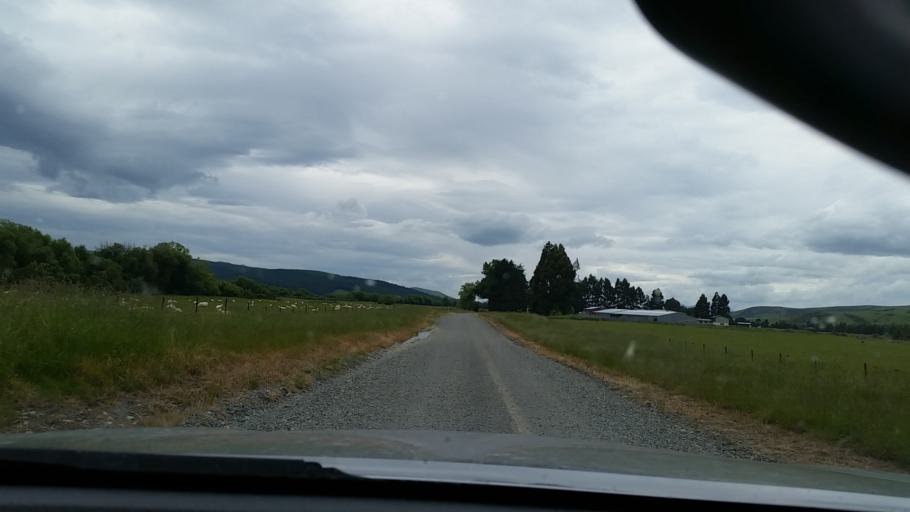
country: NZ
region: Southland
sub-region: Southland District
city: Winton
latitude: -45.8547
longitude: 168.1373
